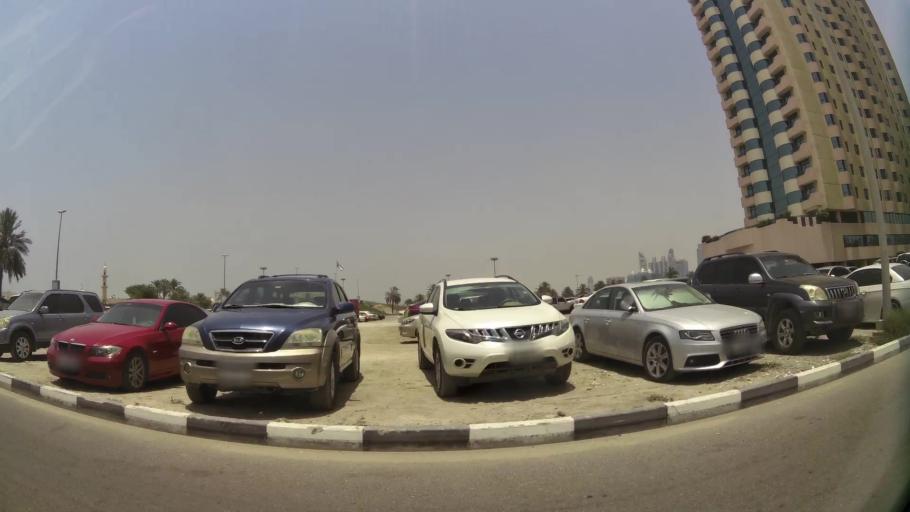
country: AE
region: Ash Shariqah
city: Sharjah
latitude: 25.3377
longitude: 55.3750
